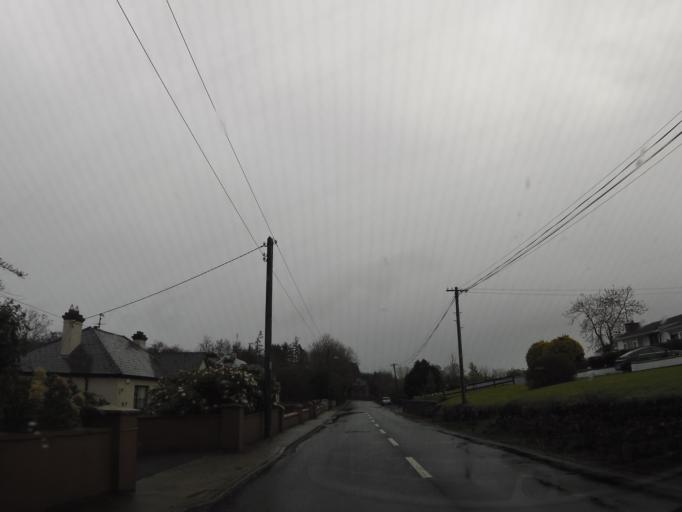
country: IE
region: Connaught
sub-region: Sligo
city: Collooney
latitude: 54.1813
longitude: -8.4993
